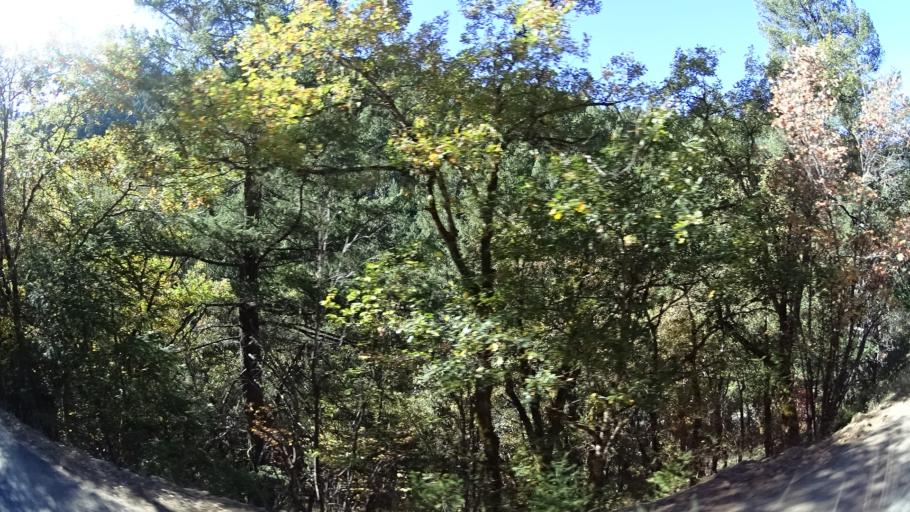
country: US
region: California
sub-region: Trinity County
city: Weaverville
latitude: 41.1421
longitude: -123.1793
